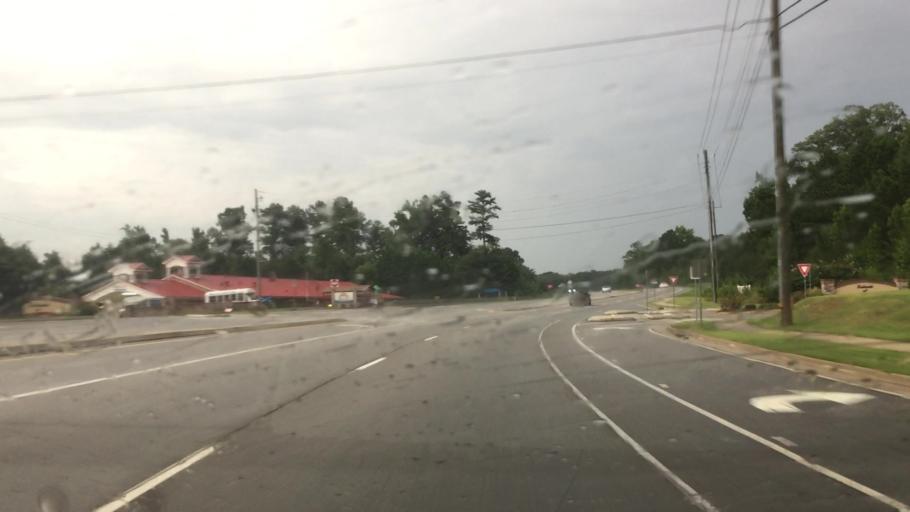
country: US
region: Georgia
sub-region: Henry County
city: Stockbridge
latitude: 33.5191
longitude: -84.1869
